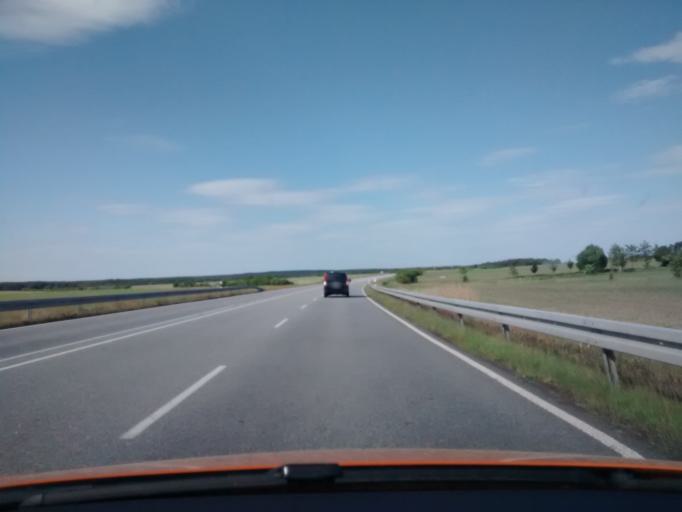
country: DE
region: Brandenburg
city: Luckenwalde
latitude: 52.1074
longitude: 13.1206
